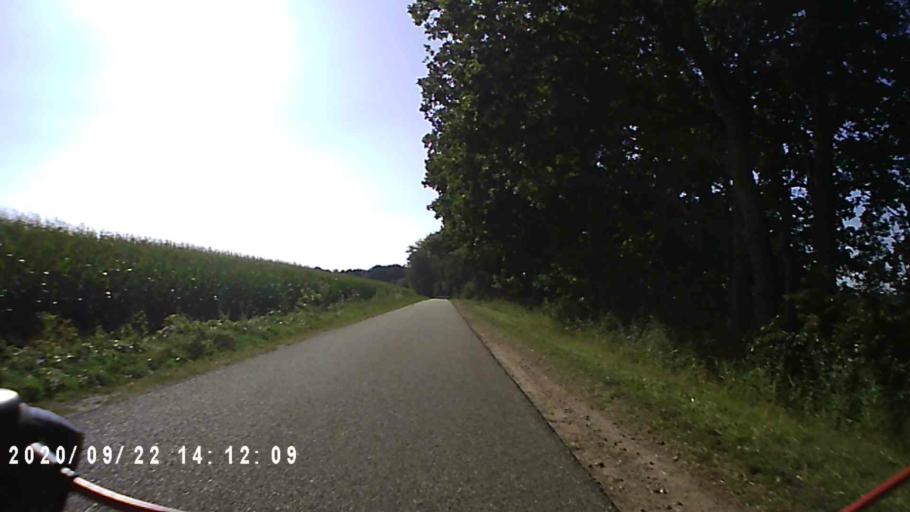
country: NL
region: Groningen
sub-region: Gemeente Leek
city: Leek
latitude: 53.0773
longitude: 6.4181
